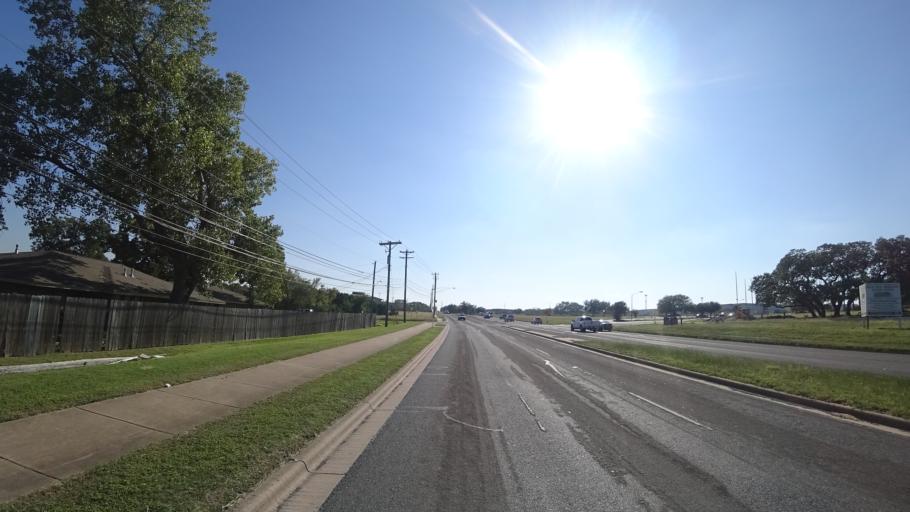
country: US
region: Texas
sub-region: Travis County
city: Austin
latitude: 30.3417
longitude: -97.6802
